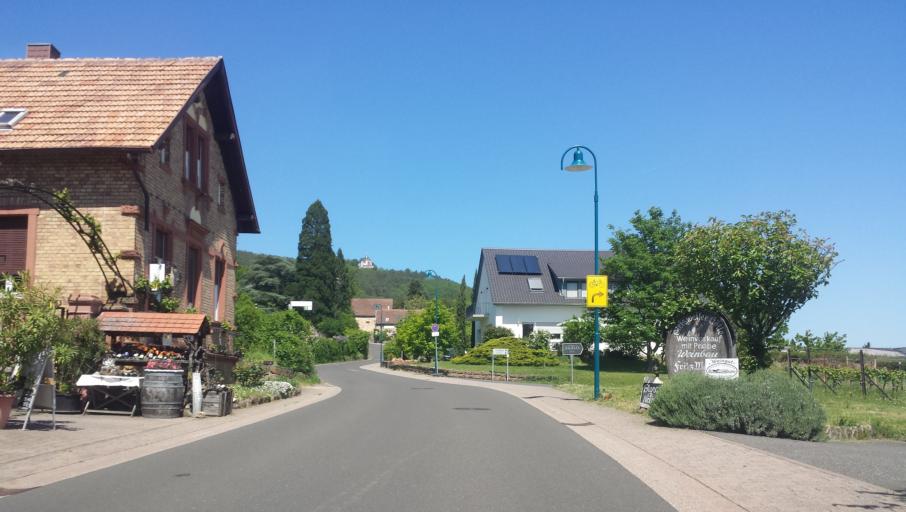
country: DE
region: Rheinland-Pfalz
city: Gleisweiler
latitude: 49.2401
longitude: 8.0679
